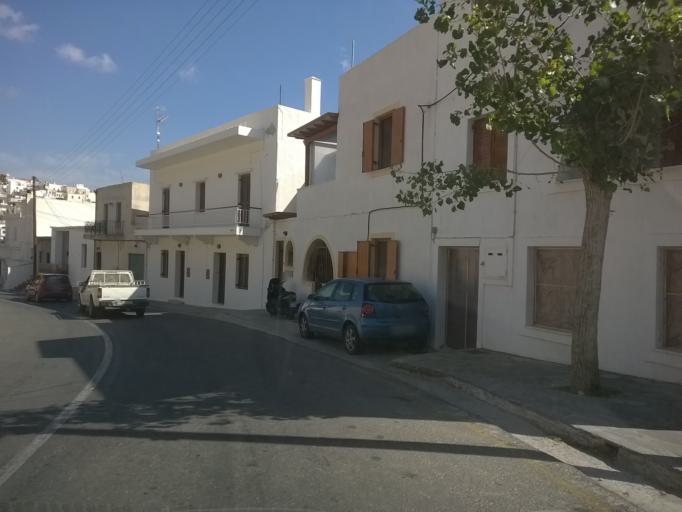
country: GR
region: South Aegean
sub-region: Nomos Kykladon
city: Filotion
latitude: 37.0678
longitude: 25.5181
